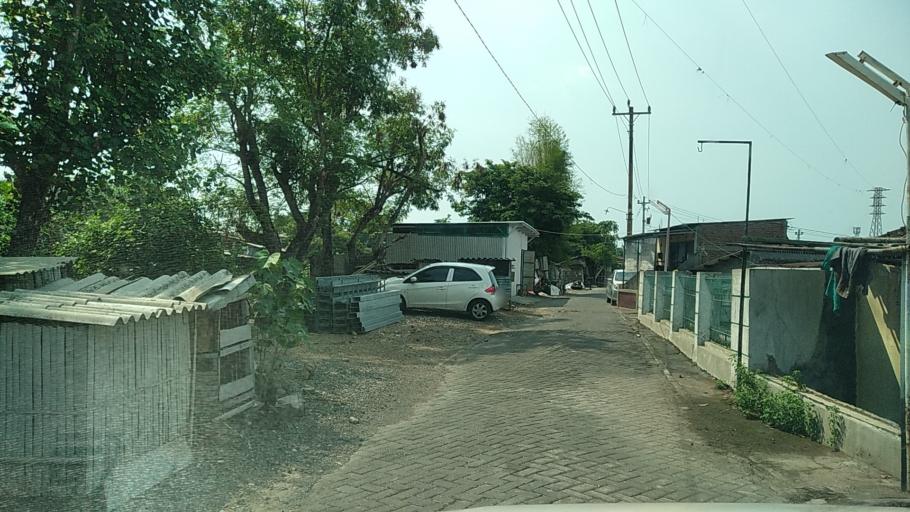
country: ID
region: Central Java
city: Semarang
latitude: -6.9993
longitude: 110.4397
